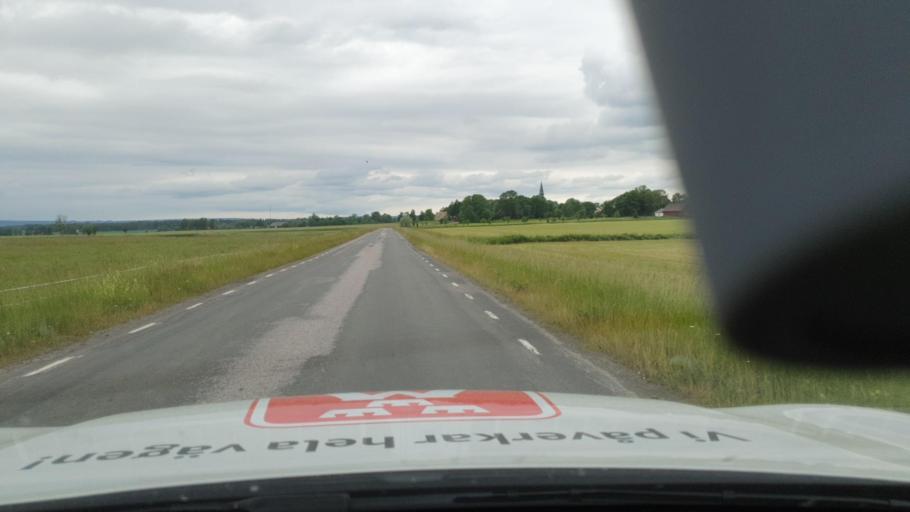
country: SE
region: Vaestra Goetaland
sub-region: Tidaholms Kommun
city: Olofstorp
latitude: 58.3302
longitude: 13.9924
